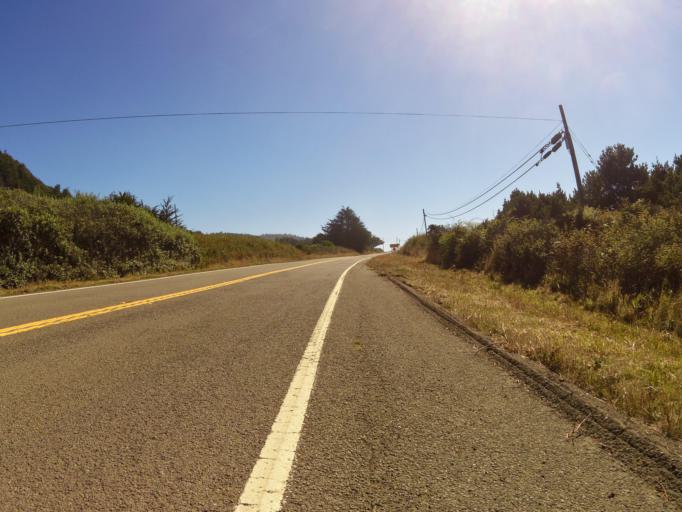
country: US
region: California
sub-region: Mendocino County
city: Fort Bragg
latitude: 39.6565
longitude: -123.7846
